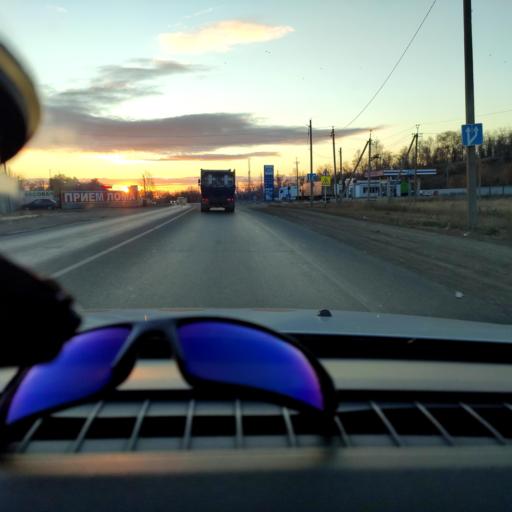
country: RU
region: Samara
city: Novokuybyshevsk
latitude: 53.0823
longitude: 50.0722
